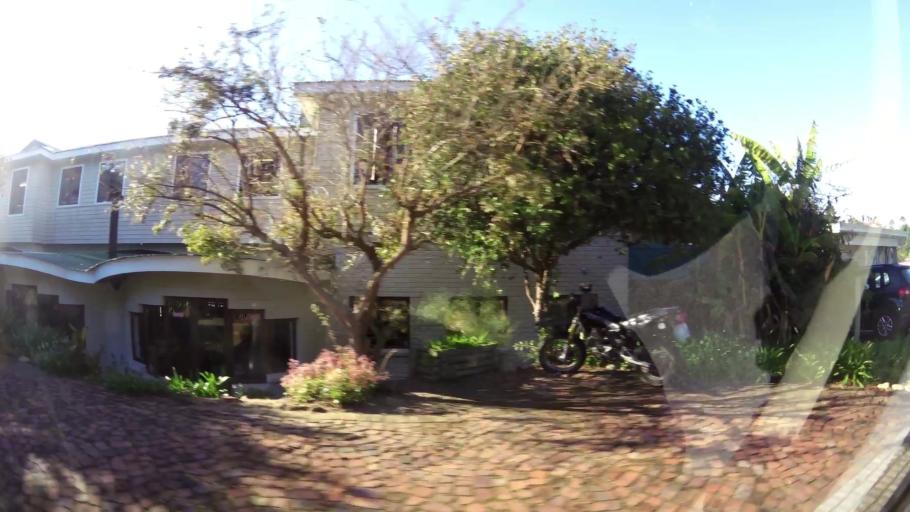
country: ZA
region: Western Cape
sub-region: Eden District Municipality
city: Knysna
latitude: -34.0327
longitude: 23.0208
